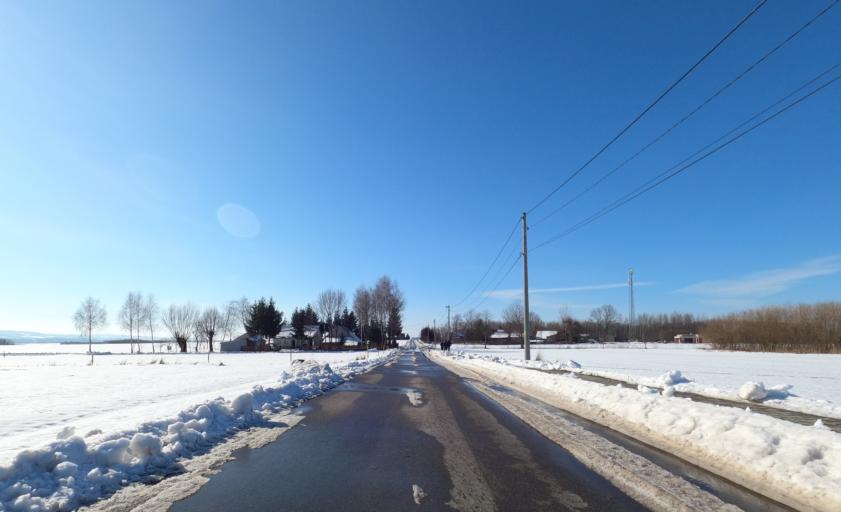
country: PL
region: Subcarpathian Voivodeship
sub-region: Powiat debicki
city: Brzeznica
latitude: 50.0849
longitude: 21.5155
